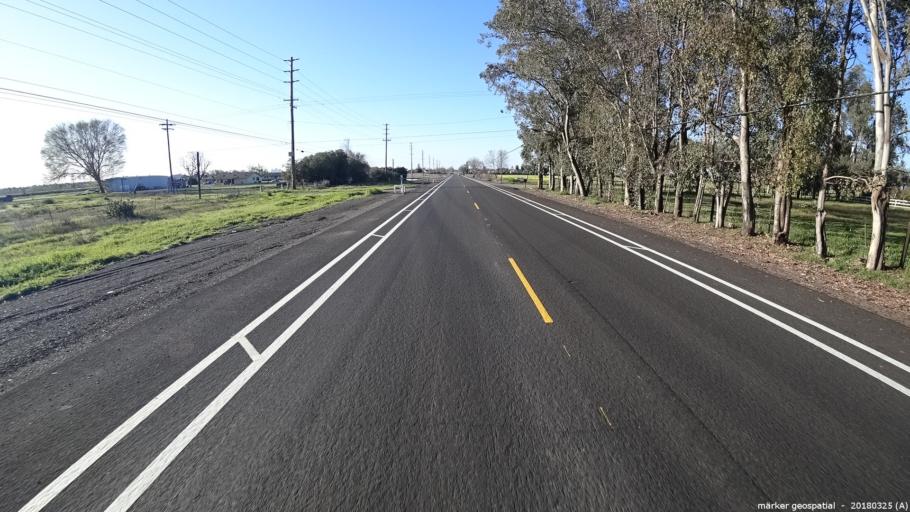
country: US
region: California
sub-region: Yolo County
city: West Sacramento
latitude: 38.6352
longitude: -121.5397
